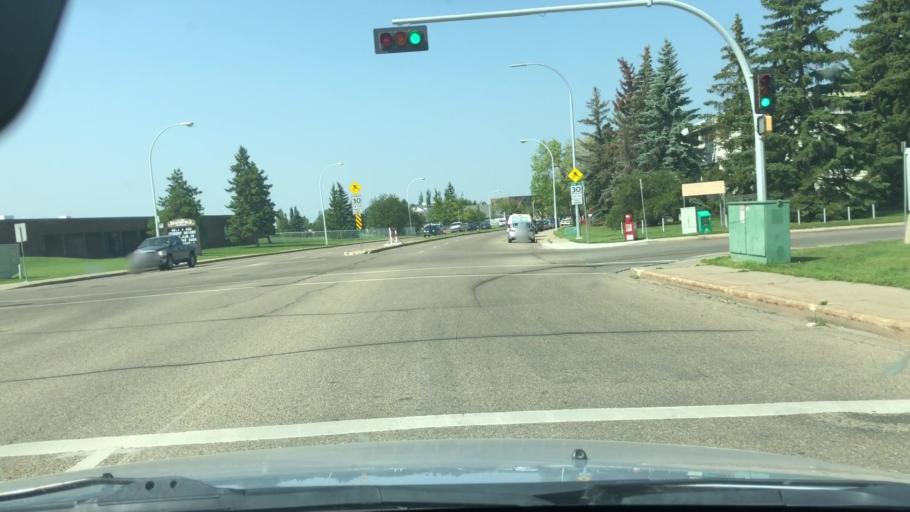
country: CA
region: Alberta
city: Edmonton
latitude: 53.6060
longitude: -113.4763
